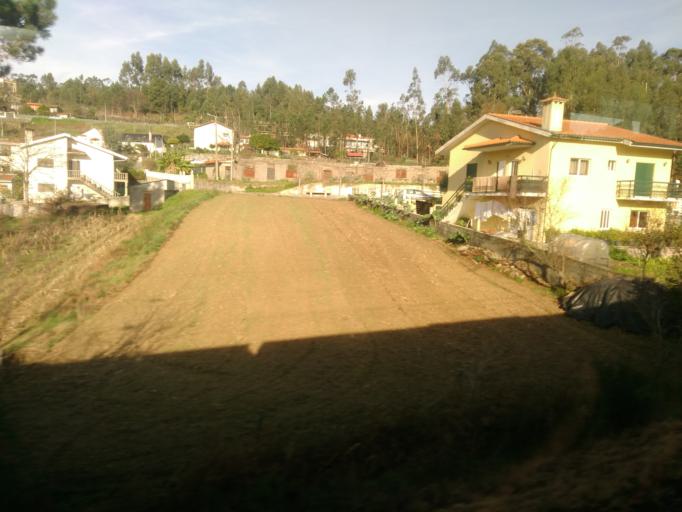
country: PT
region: Braga
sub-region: Braga
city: Oliveira
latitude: 41.4997
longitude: -8.4940
